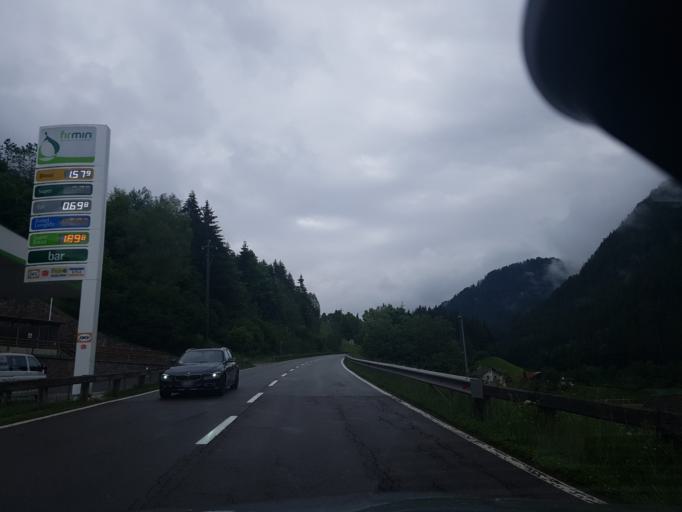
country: IT
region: Trentino-Alto Adige
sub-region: Bolzano
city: Ortisei
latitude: 46.5660
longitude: 11.6905
